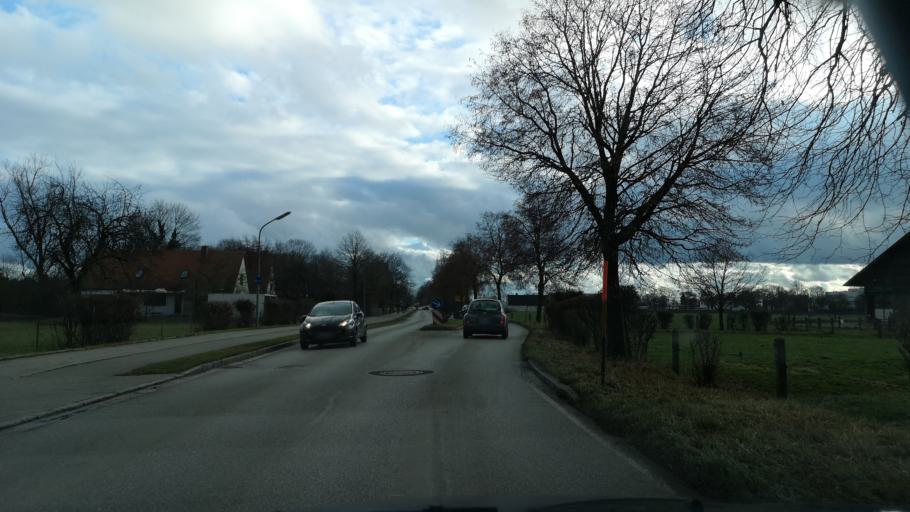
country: DE
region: Bavaria
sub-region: Upper Bavaria
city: Kirchheim bei Muenchen
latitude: 48.1687
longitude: 11.7801
